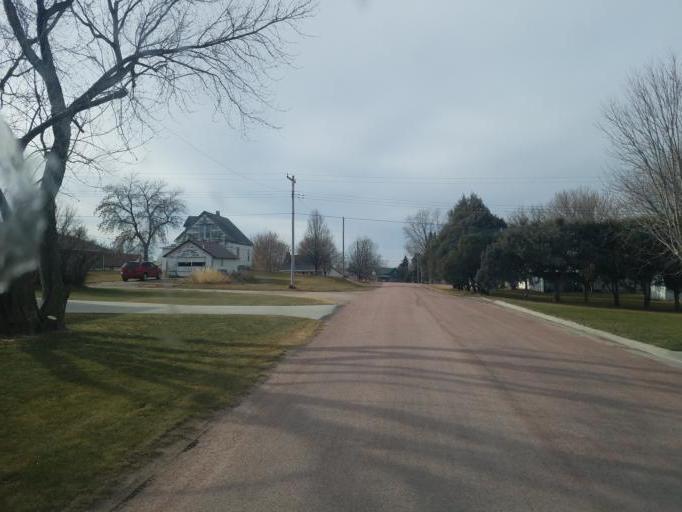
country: US
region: Nebraska
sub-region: Knox County
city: Creighton
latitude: 42.4599
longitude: -97.9065
